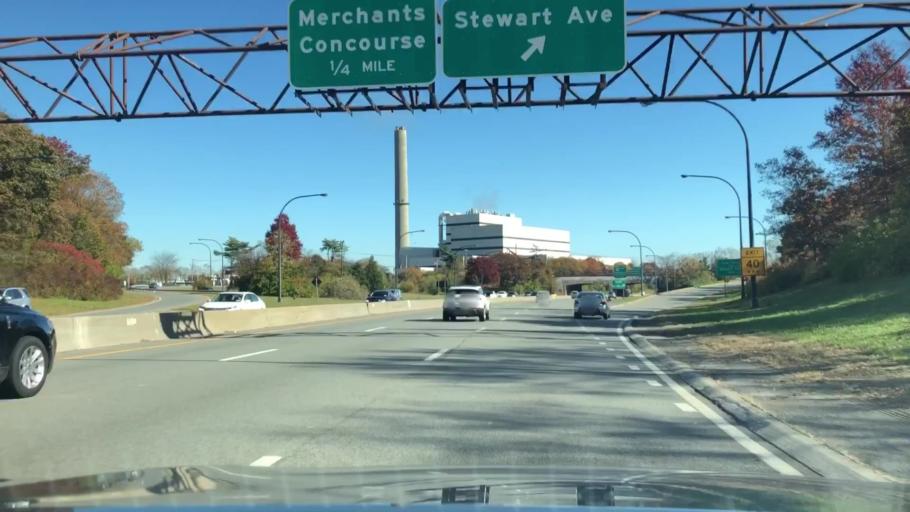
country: US
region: New York
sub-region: Nassau County
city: East Garden City
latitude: 40.7372
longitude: -73.5967
